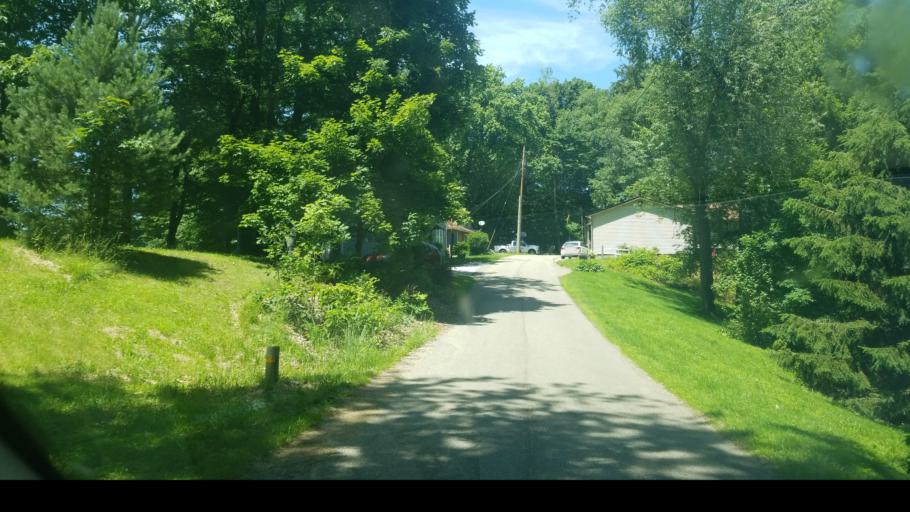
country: US
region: Ohio
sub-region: Mahoning County
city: Sebring
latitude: 40.8515
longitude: -80.9917
